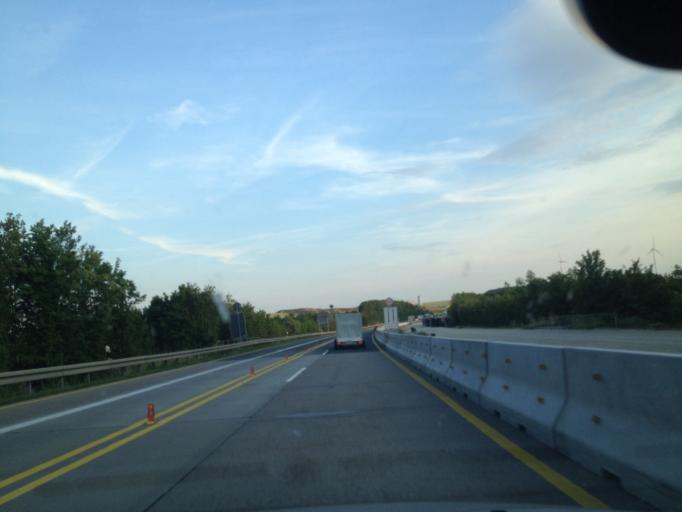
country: DE
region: Bavaria
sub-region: Regierungsbezirk Mittelfranken
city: Gollhofen
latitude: 49.5730
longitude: 10.1726
